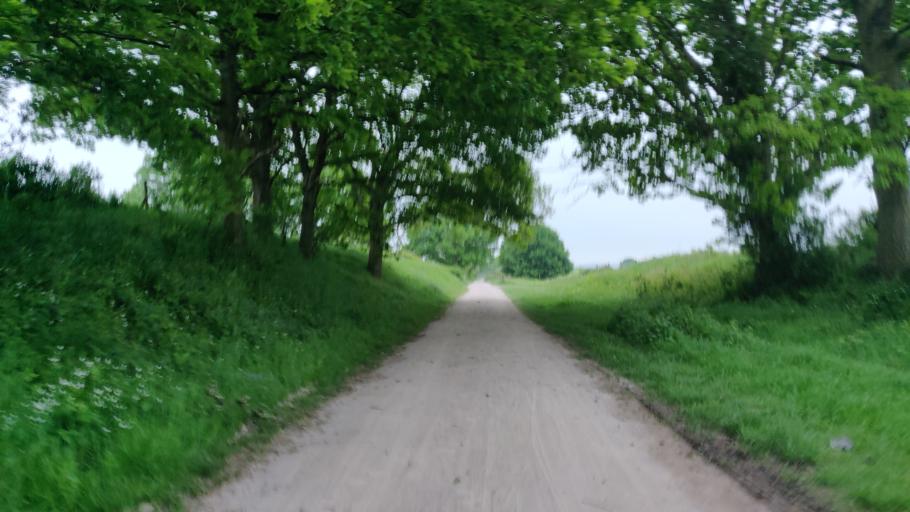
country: GB
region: England
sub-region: West Sussex
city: Partridge Green
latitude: 50.9825
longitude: -0.3152
